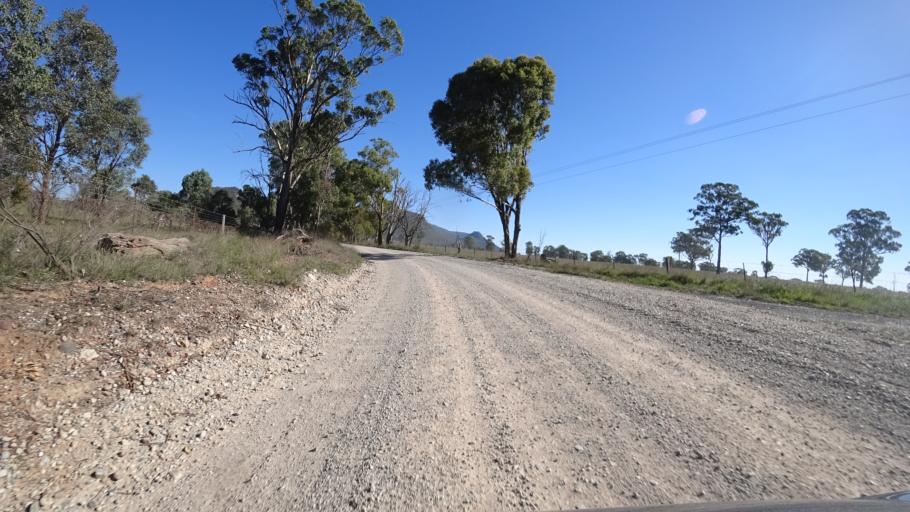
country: AU
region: New South Wales
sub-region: Mid-Western Regional
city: Kandos
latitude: -32.8292
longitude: 150.0164
